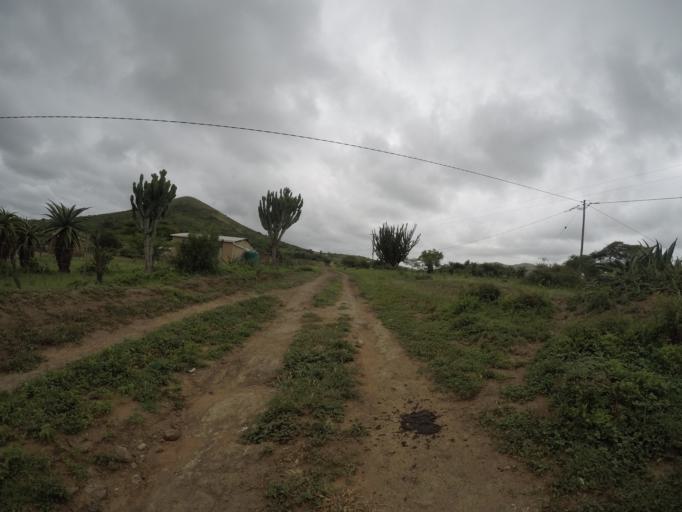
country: ZA
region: KwaZulu-Natal
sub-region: uThungulu District Municipality
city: Empangeni
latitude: -28.6074
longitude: 31.8592
